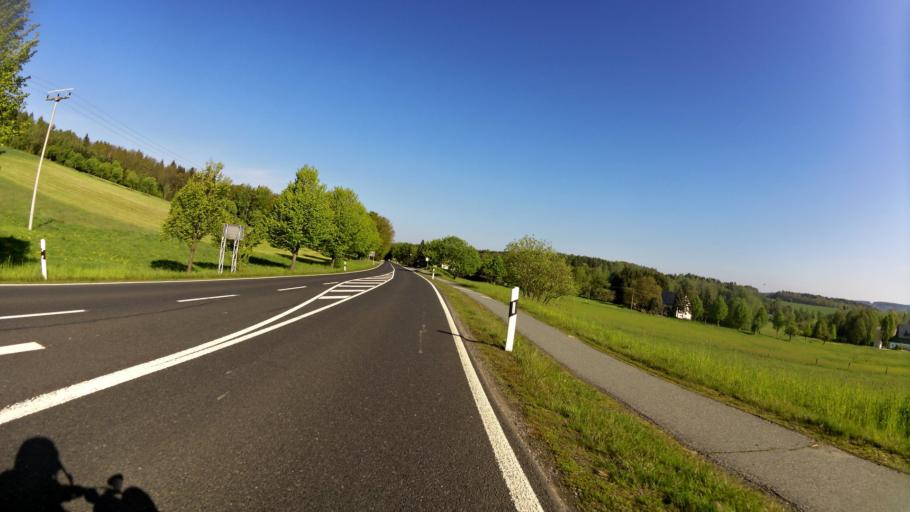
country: DE
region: Saxony
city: Sebnitz
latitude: 50.9985
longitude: 14.2452
